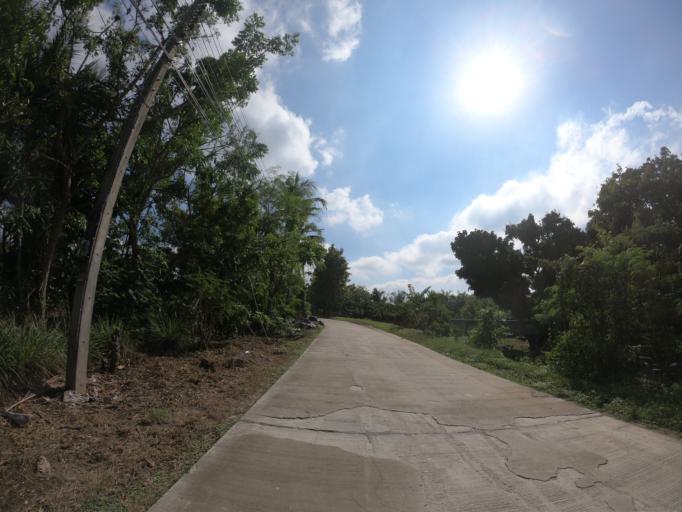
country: TH
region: Chiang Mai
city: Saraphi
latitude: 18.7156
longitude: 99.0201
